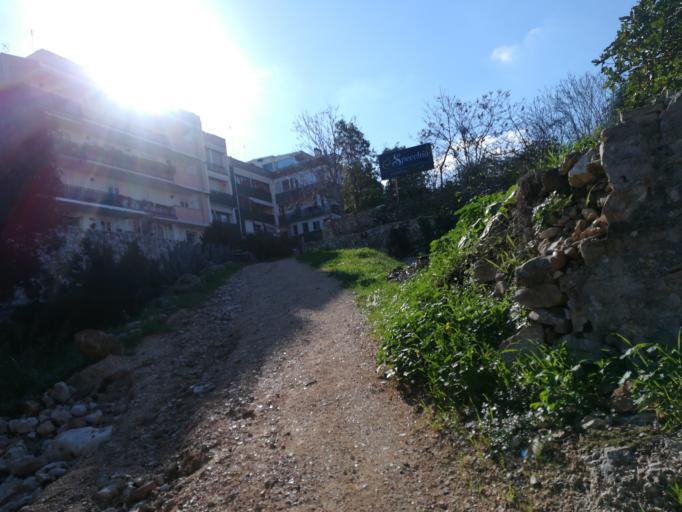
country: IT
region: Apulia
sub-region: Provincia di Bari
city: Polignano a Mare
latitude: 40.9949
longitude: 17.2174
